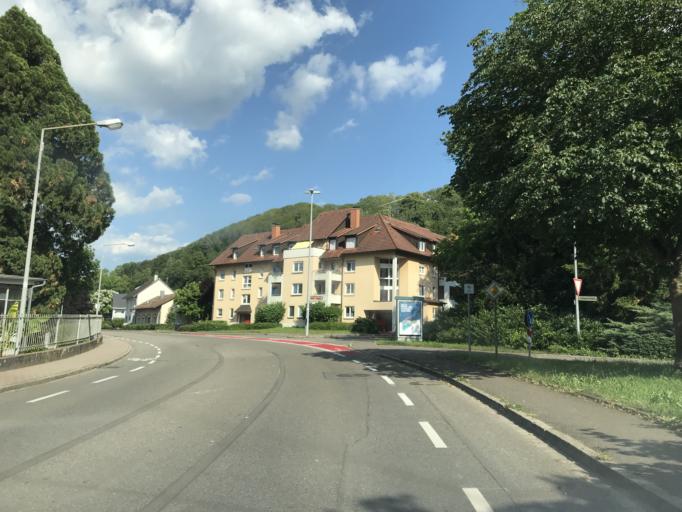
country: DE
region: Baden-Wuerttemberg
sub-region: Freiburg Region
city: Loerrach
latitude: 47.6362
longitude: 7.6972
